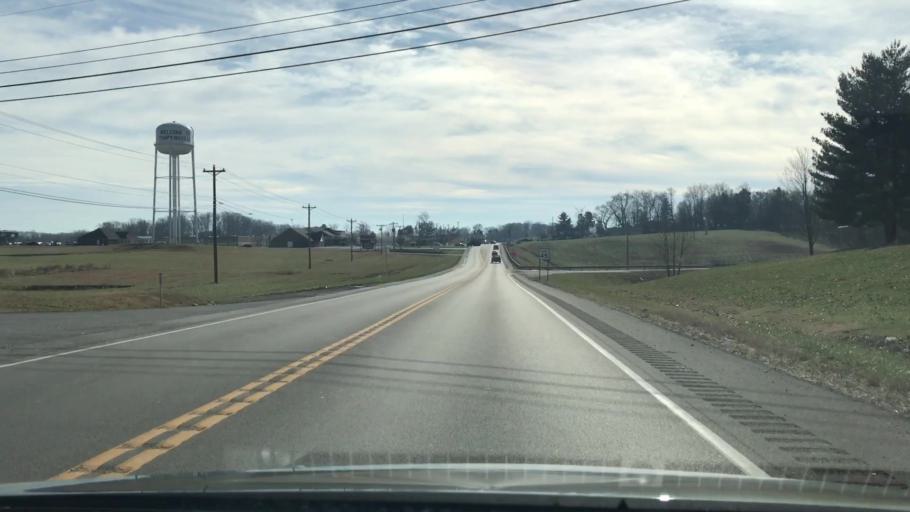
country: US
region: Kentucky
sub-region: Monroe County
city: Tompkinsville
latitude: 36.7286
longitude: -85.6875
